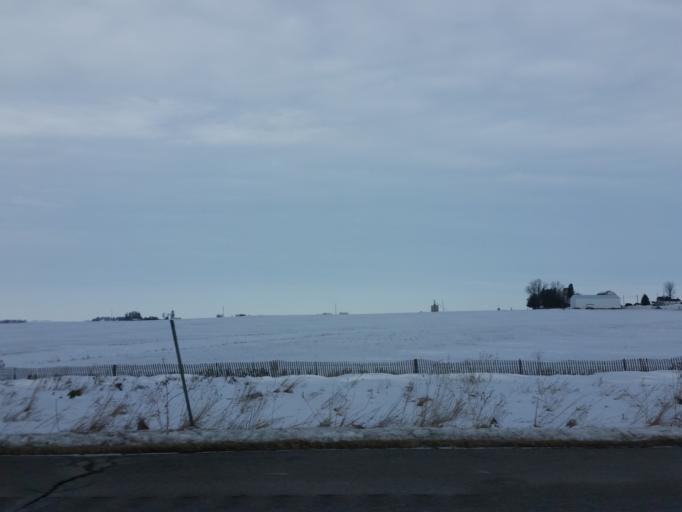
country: US
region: Iowa
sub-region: Delaware County
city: Manchester
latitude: 42.4646
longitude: -91.5931
